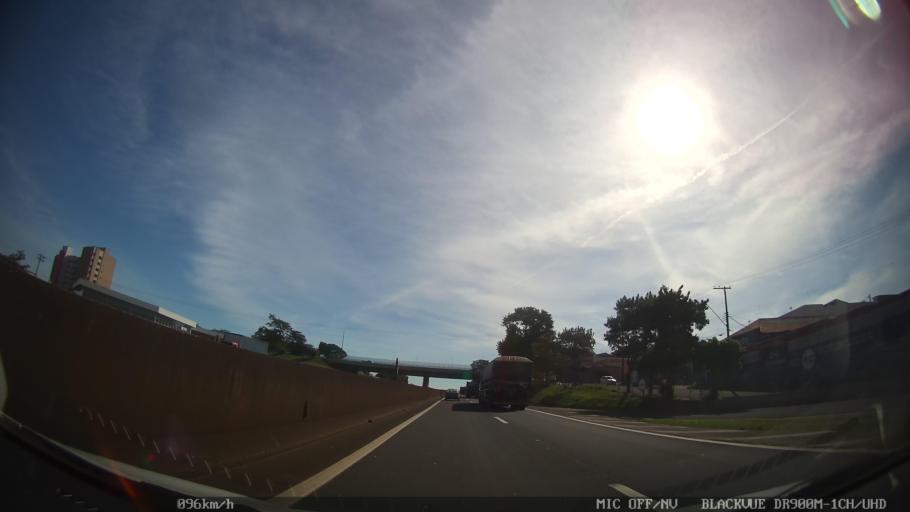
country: BR
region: Sao Paulo
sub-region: Araras
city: Araras
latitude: -22.3584
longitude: -47.3947
